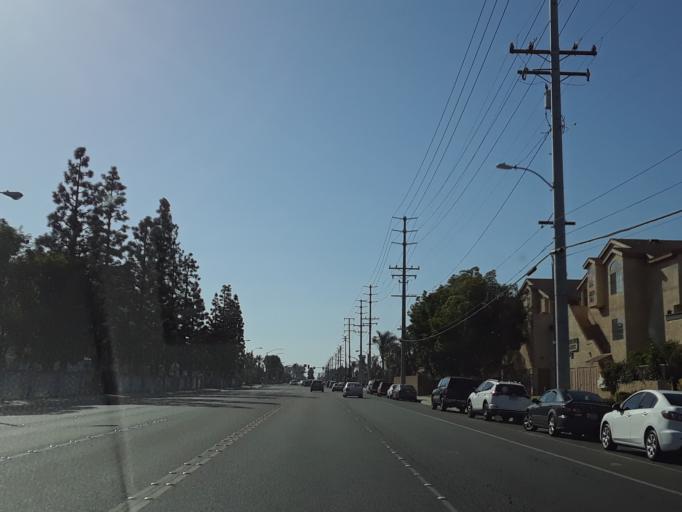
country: US
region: California
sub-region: Orange County
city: Huntington Beach
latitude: 33.6867
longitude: -117.9856
